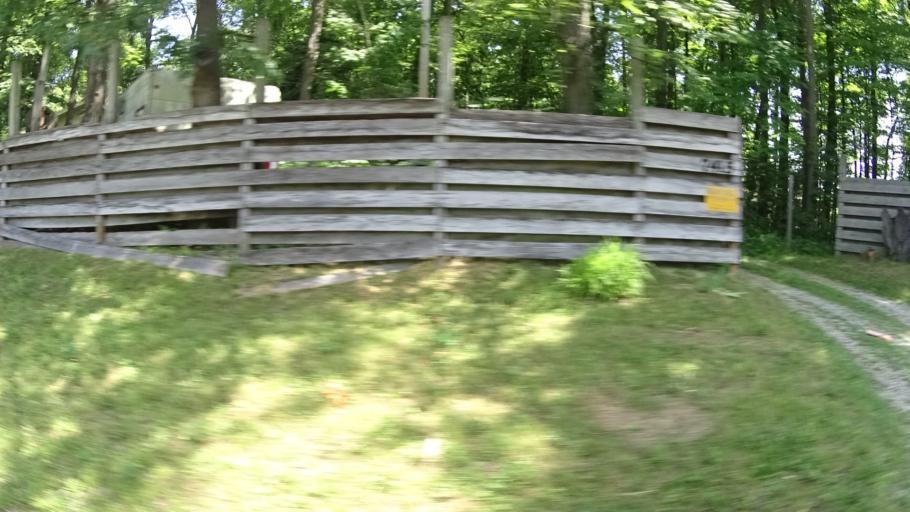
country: US
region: Ohio
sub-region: Erie County
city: Huron
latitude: 41.3604
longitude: -82.4891
